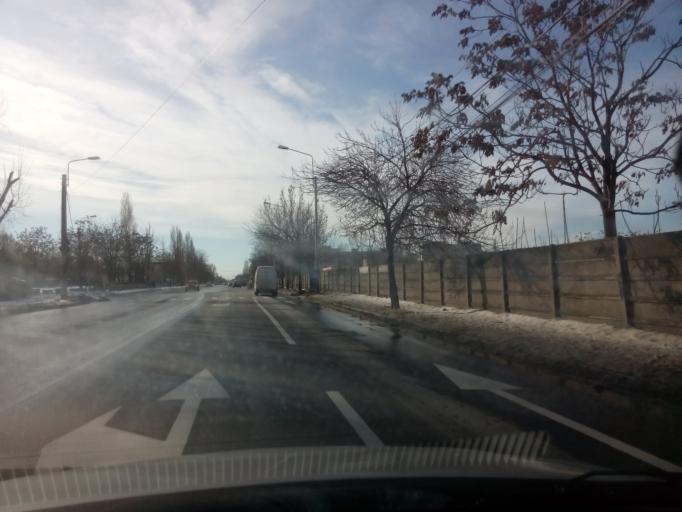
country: RO
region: Ilfov
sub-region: Comuna Popesti-Leordeni
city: Popesti-Leordeni
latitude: 44.3896
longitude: 26.1422
